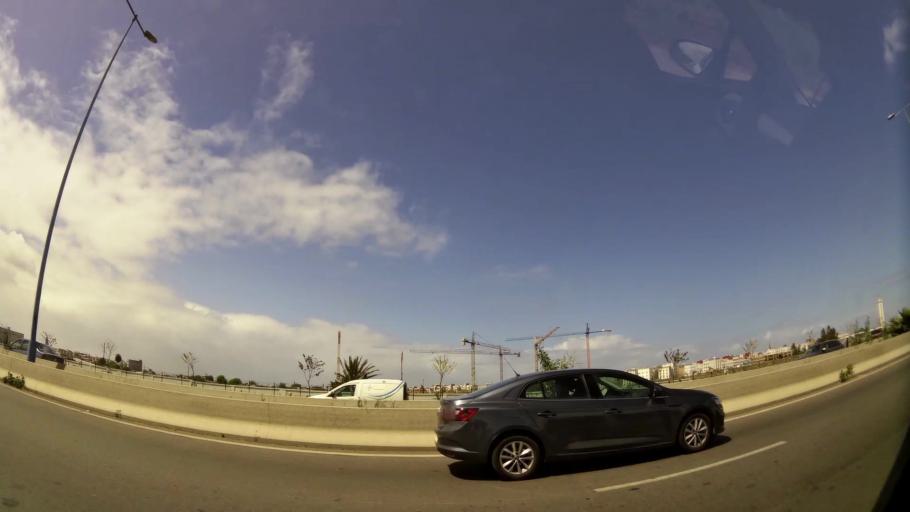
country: MA
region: Grand Casablanca
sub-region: Mediouna
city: Tit Mellil
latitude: 33.5980
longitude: -7.5128
